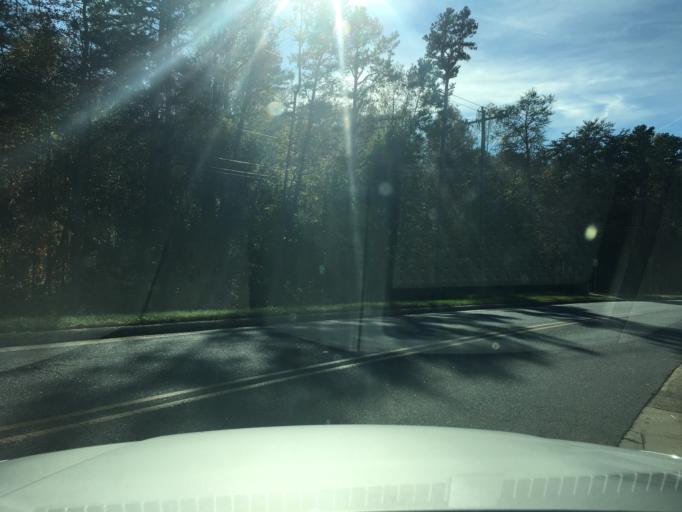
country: US
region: North Carolina
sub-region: Catawba County
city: Conover
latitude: 35.7121
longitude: -81.2691
